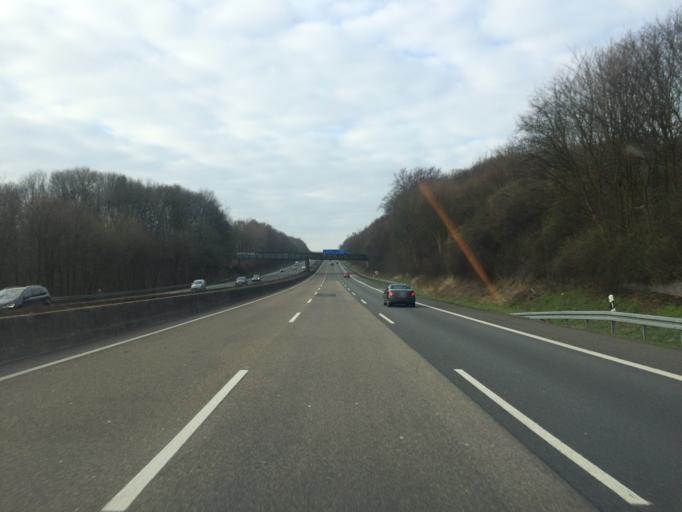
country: DE
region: North Rhine-Westphalia
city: Burscheid
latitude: 51.0954
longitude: 7.1392
